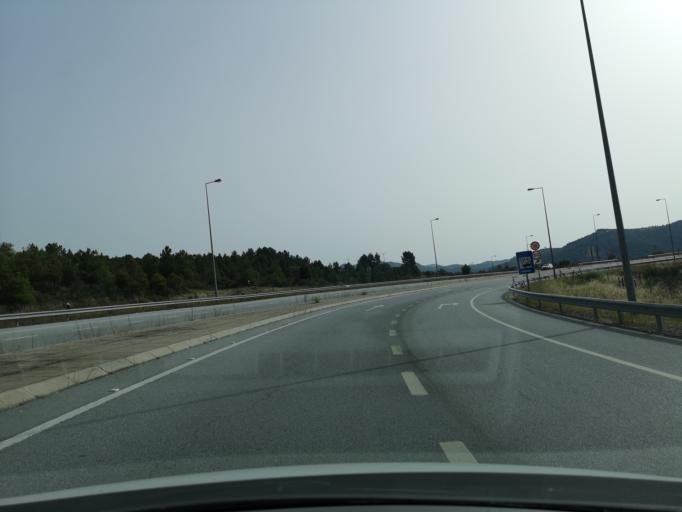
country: PT
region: Castelo Branco
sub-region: Belmonte
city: Belmonte
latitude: 40.3756
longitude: -7.3169
